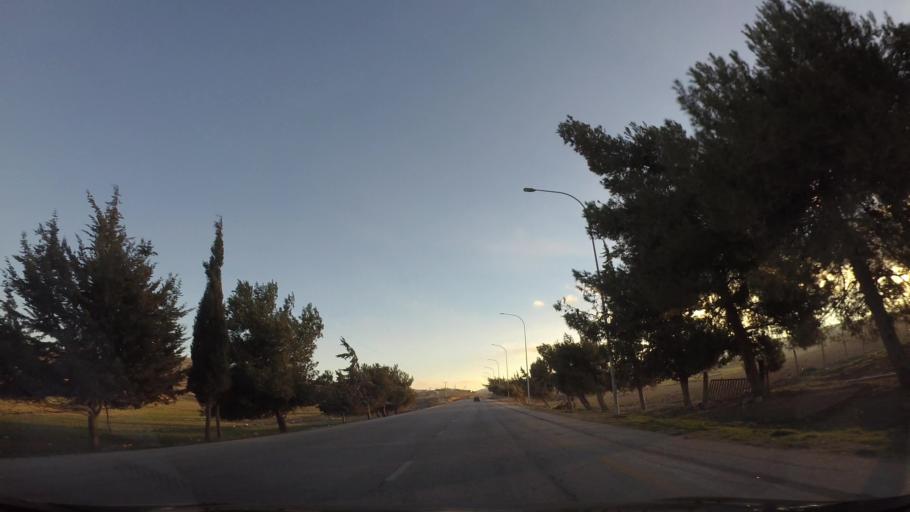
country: JO
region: Ma'an
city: Petra
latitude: 30.4477
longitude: 35.5239
